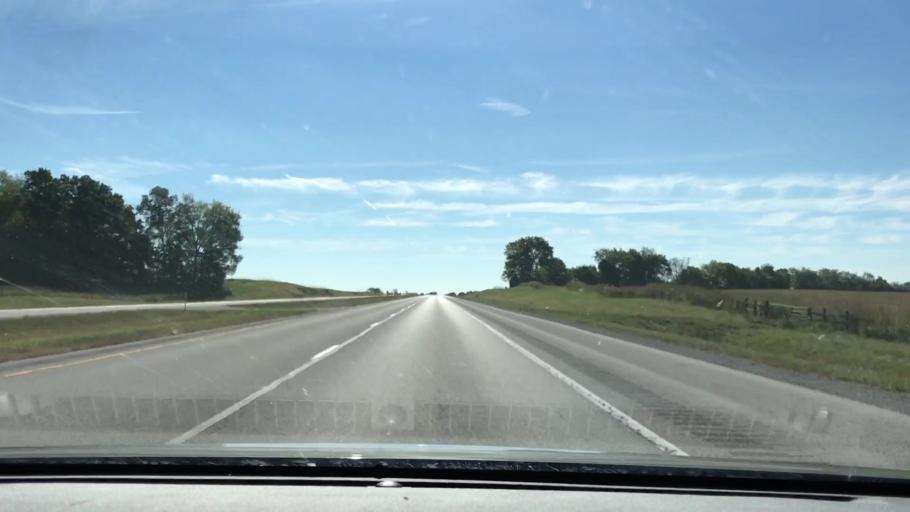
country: US
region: Kentucky
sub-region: Todd County
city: Elkton
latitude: 36.8203
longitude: -87.1447
